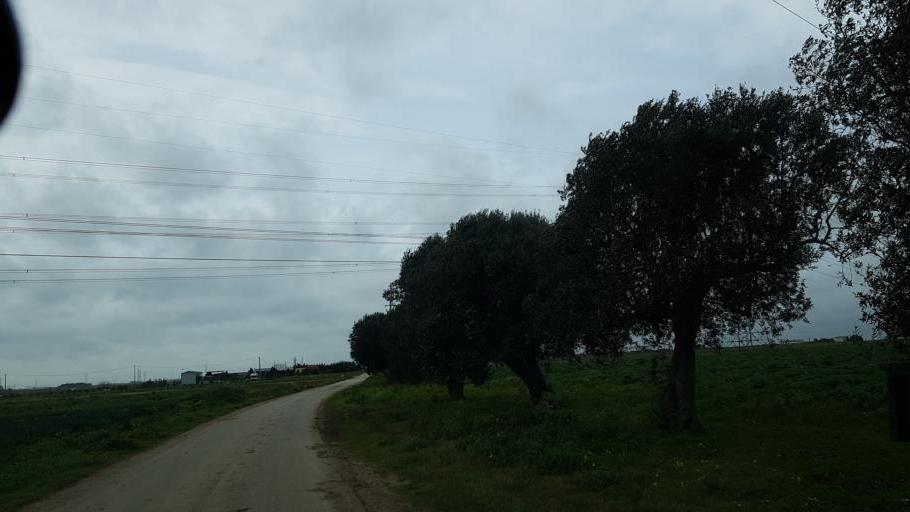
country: IT
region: Apulia
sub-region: Provincia di Brindisi
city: La Rosa
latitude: 40.5991
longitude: 17.9211
